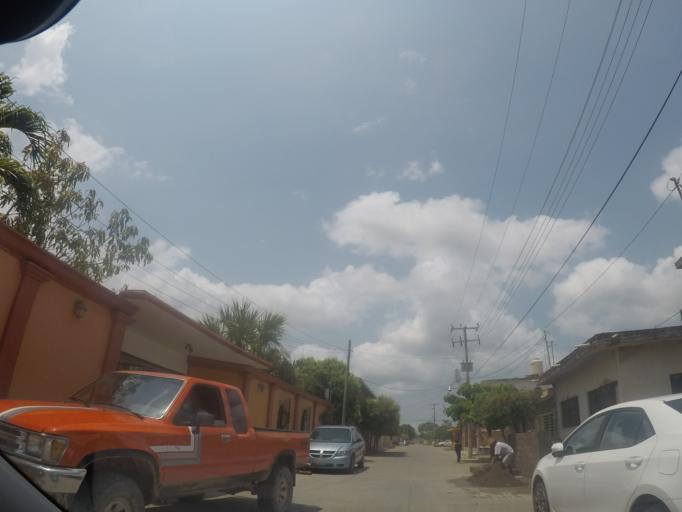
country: MX
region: Oaxaca
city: El Espinal
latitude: 16.5518
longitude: -94.9483
